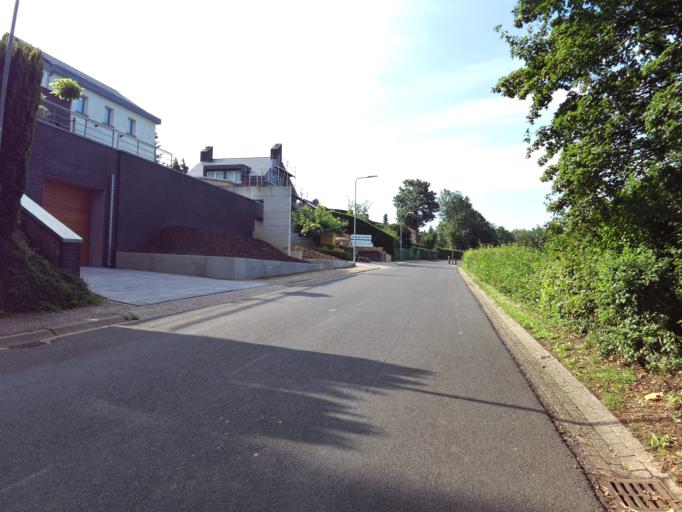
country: NL
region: Limburg
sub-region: Gemeente Voerendaal
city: Klimmen
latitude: 50.8711
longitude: 5.8841
